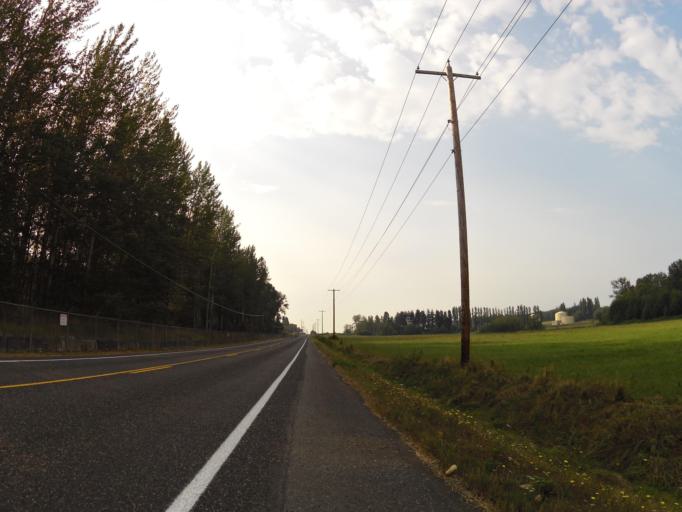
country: US
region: Washington
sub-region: Whatcom County
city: Birch Bay
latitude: 48.8915
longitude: -122.7489
